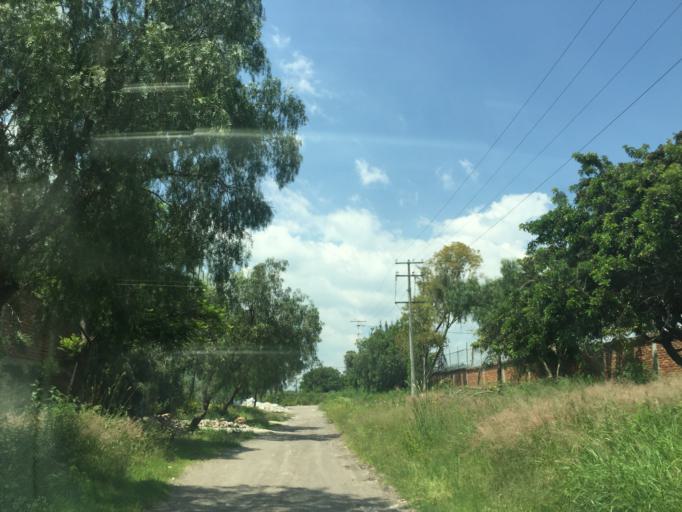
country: MX
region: Guanajuato
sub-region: Leon
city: La Ermita
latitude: 21.1589
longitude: -101.7217
